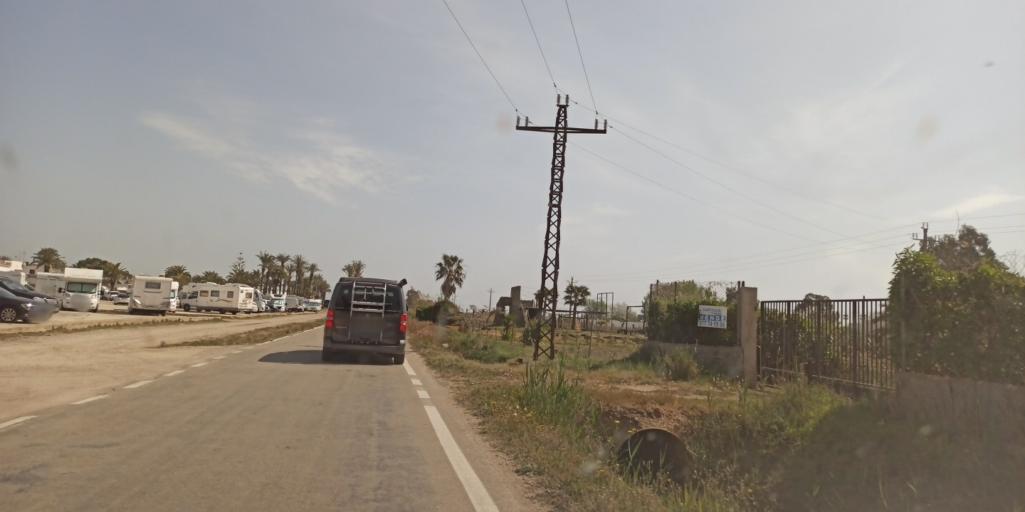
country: ES
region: Catalonia
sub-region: Provincia de Tarragona
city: Deltebre
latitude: 40.6435
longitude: 0.6840
